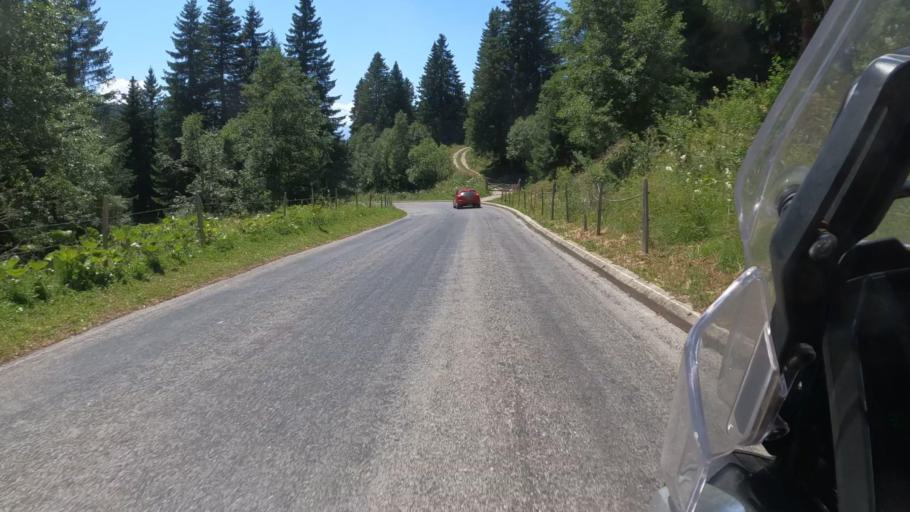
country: CH
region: Vaud
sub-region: Aigle District
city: Villars-sur-Ollon
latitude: 46.3134
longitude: 7.1066
